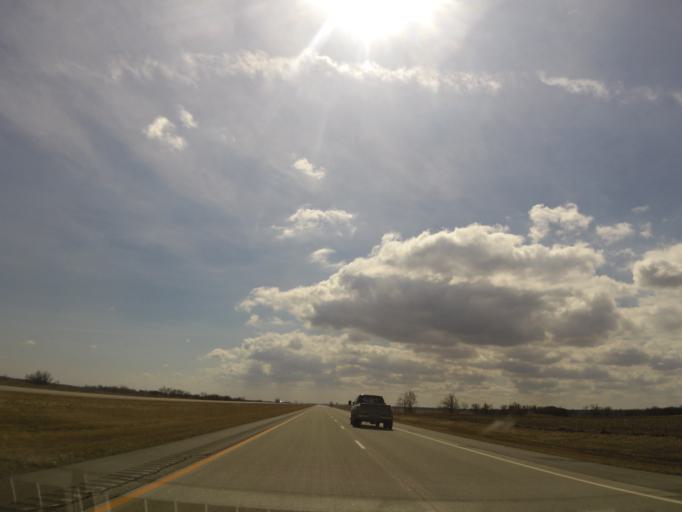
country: US
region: South Dakota
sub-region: Roberts County
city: Sisseton
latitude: 45.4878
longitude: -96.9896
